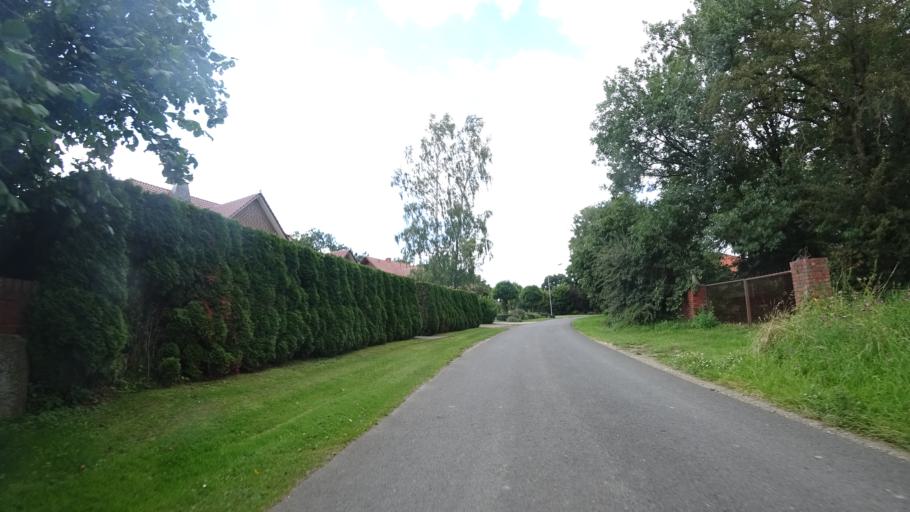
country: DE
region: Lower Saxony
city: Raddestorf
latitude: 52.4575
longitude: 9.0232
